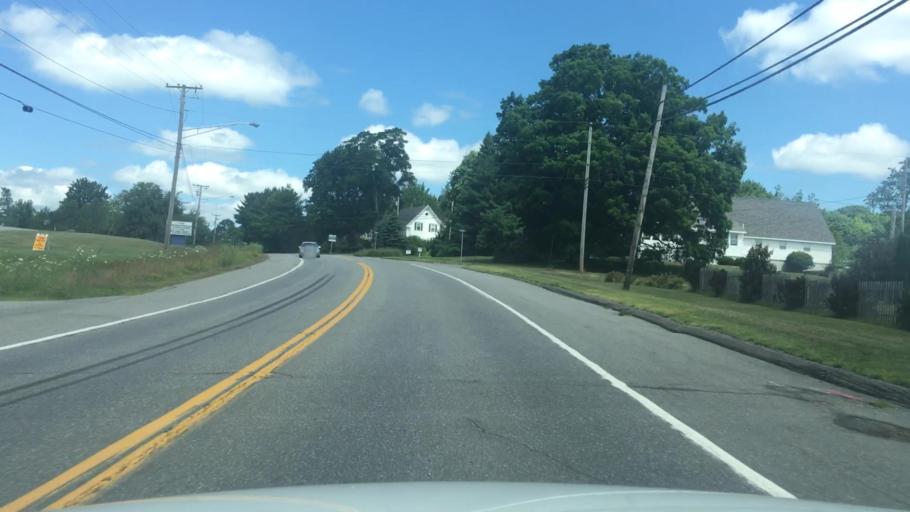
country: US
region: Maine
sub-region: Waldo County
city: Belfast
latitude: 44.3977
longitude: -68.9873
